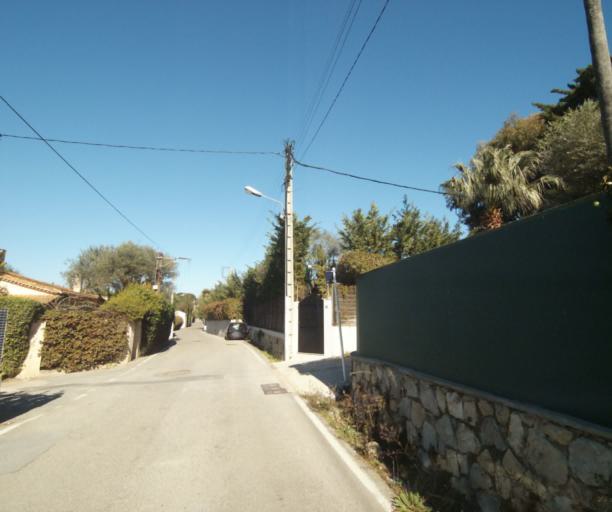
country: FR
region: Provence-Alpes-Cote d'Azur
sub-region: Departement des Alpes-Maritimes
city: Antibes
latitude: 43.5568
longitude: 7.1247
